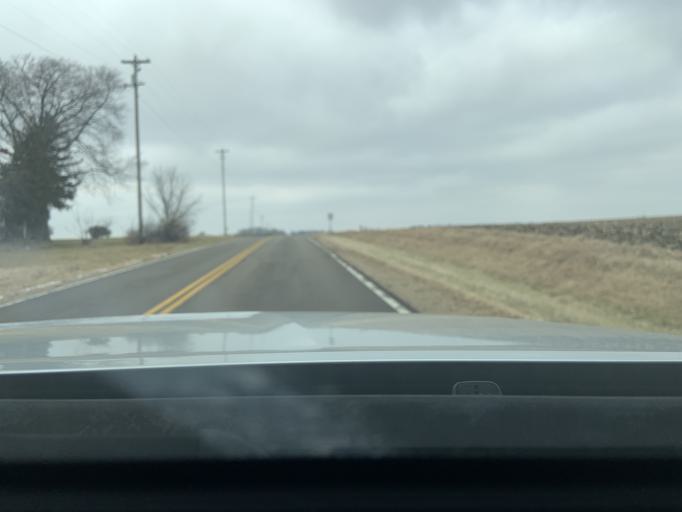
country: US
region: Illinois
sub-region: LaSalle County
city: Seneca
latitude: 41.3796
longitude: -88.6132
